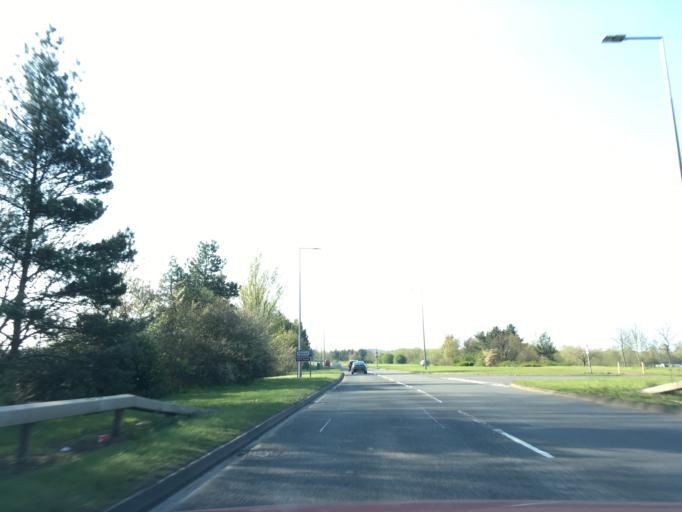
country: GB
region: England
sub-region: Milton Keynes
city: Broughton
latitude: 52.0598
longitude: -0.7139
